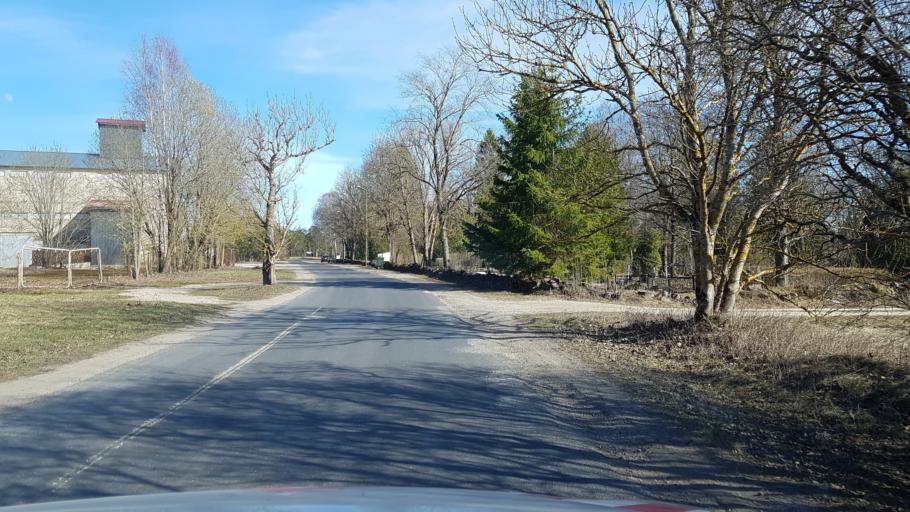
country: EE
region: Harju
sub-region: Nissi vald
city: Riisipere
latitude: 59.1006
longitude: 24.3169
